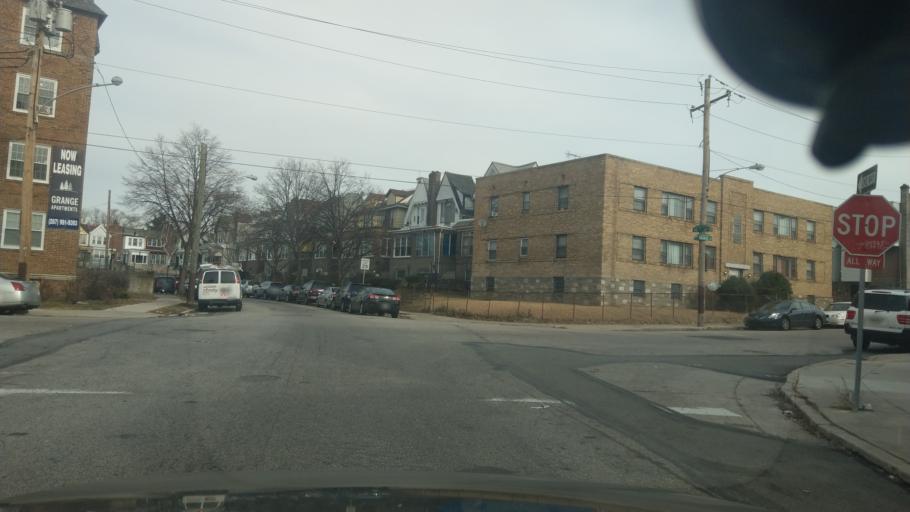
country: US
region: Pennsylvania
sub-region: Montgomery County
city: Wyncote
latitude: 40.0414
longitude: -75.1472
